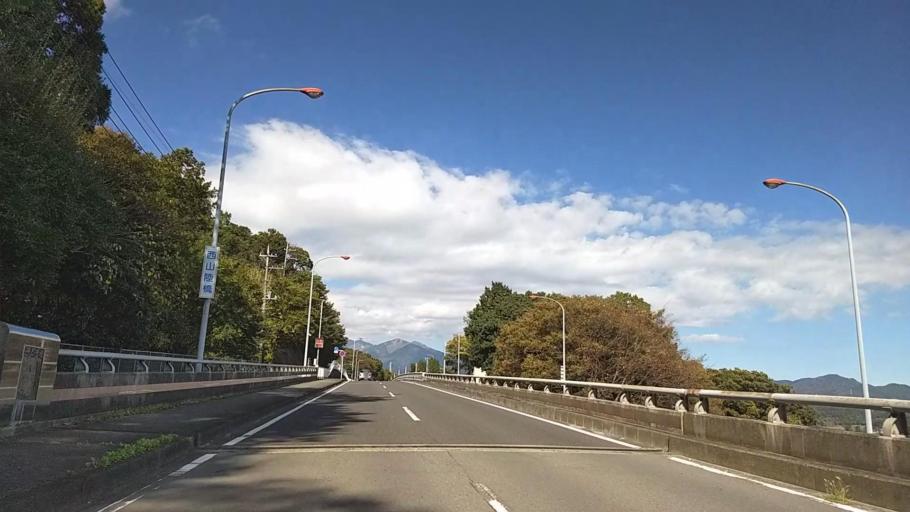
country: JP
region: Kanagawa
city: Ninomiya
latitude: 35.3328
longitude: 139.2310
